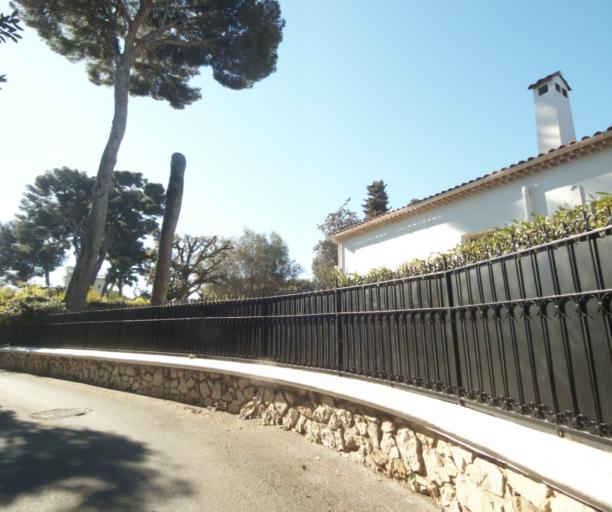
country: FR
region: Provence-Alpes-Cote d'Azur
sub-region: Departement des Alpes-Maritimes
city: Antibes
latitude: 43.5643
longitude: 7.1230
